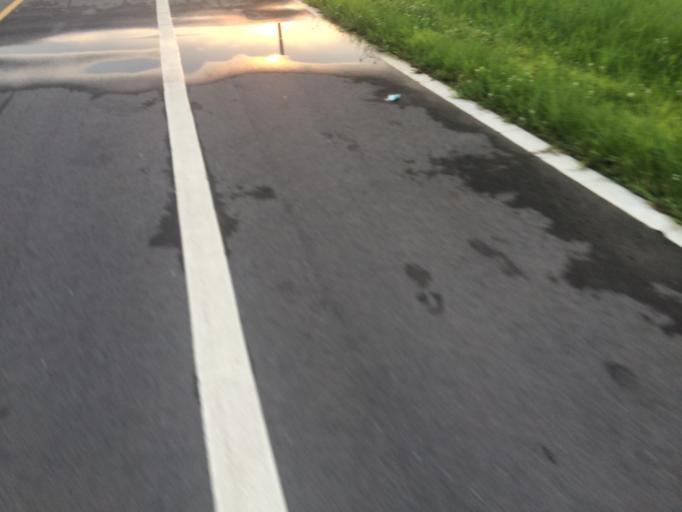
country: TW
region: Taipei
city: Taipei
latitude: 25.0763
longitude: 121.5548
